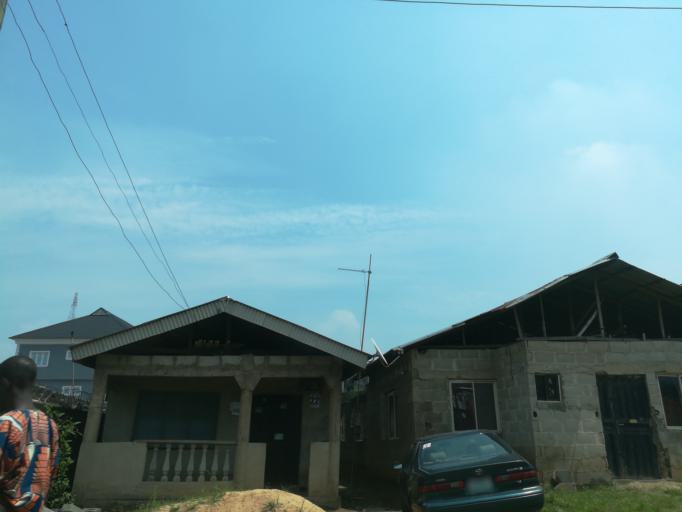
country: NG
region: Lagos
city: Ikorodu
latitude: 6.6219
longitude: 3.4914
